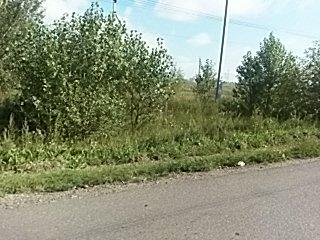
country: RU
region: Krasnoyarskiy
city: Berezovka
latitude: 56.0856
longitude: 93.0493
